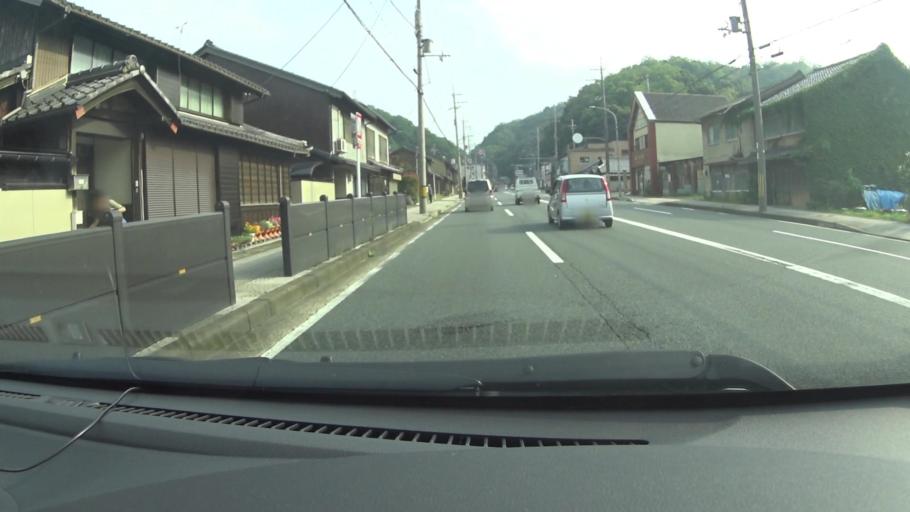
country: JP
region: Kyoto
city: Maizuru
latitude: 35.4688
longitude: 135.3649
